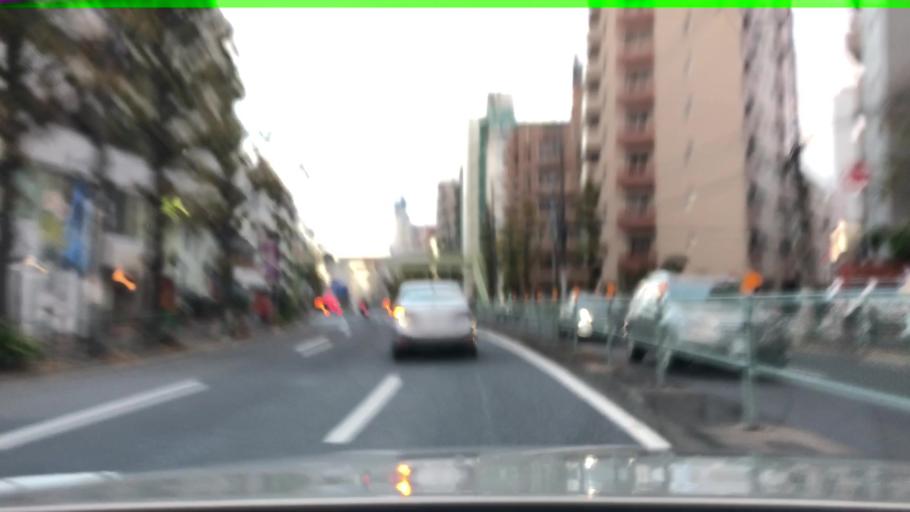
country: JP
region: Tokyo
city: Tokyo
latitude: 35.6140
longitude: 139.6671
